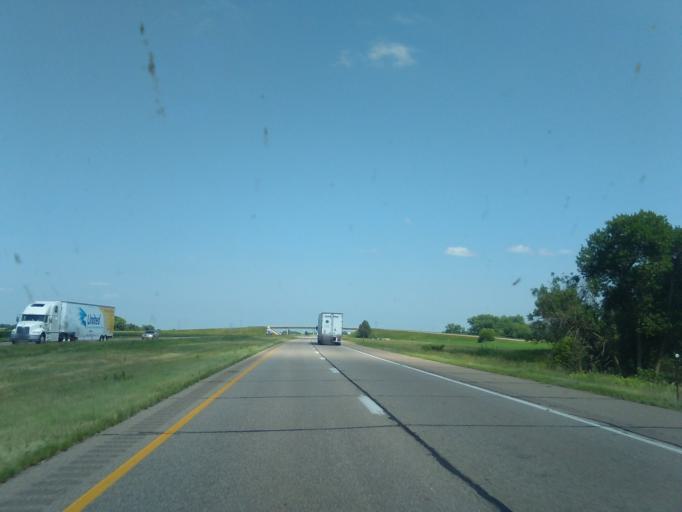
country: US
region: Nebraska
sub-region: Phelps County
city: Holdrege
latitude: 40.6908
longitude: -99.3474
